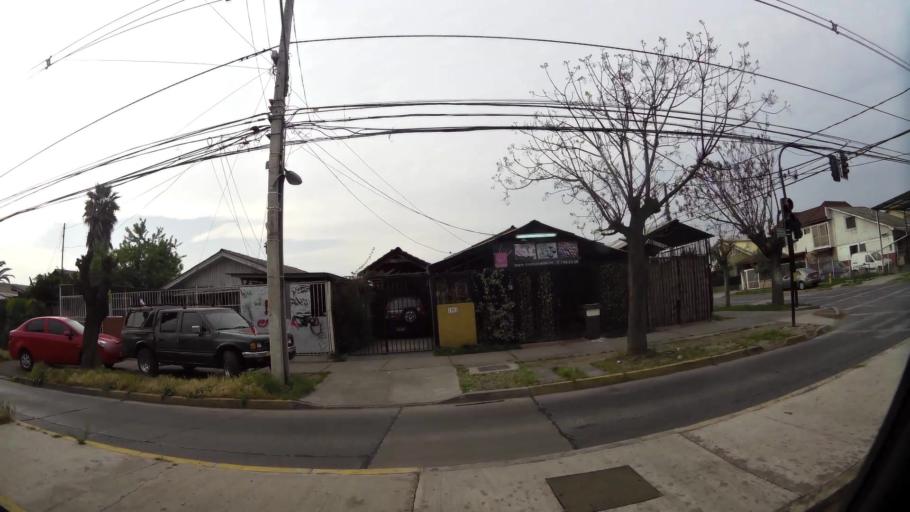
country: CL
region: Santiago Metropolitan
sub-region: Provincia de Santiago
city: Lo Prado
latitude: -33.5214
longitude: -70.7711
